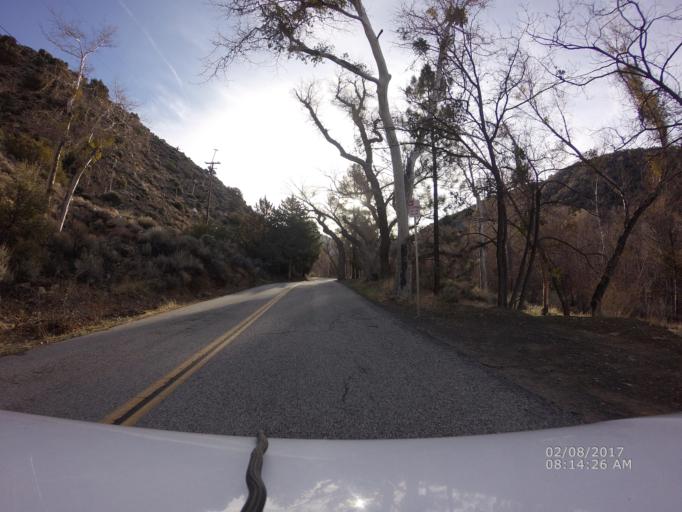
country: US
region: California
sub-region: Los Angeles County
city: Littlerock
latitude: 34.4158
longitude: -117.8350
